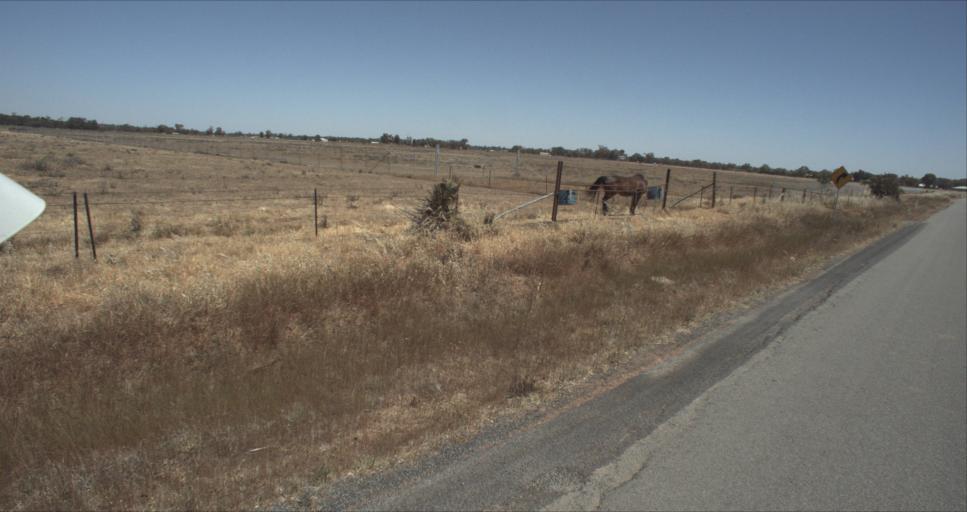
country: AU
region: New South Wales
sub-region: Leeton
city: Leeton
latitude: -34.5441
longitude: 146.4282
